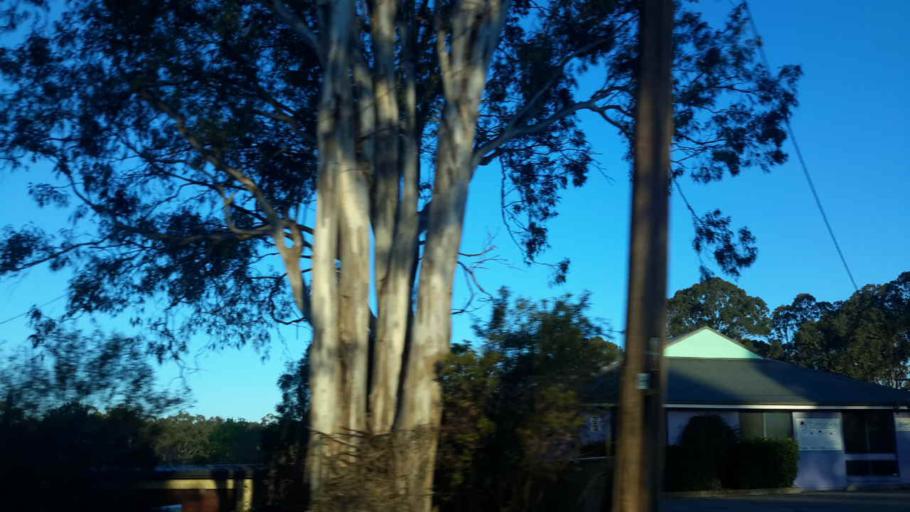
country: AU
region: New South Wales
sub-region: Wollondilly
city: Douglas Park
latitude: -34.2353
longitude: 150.7296
